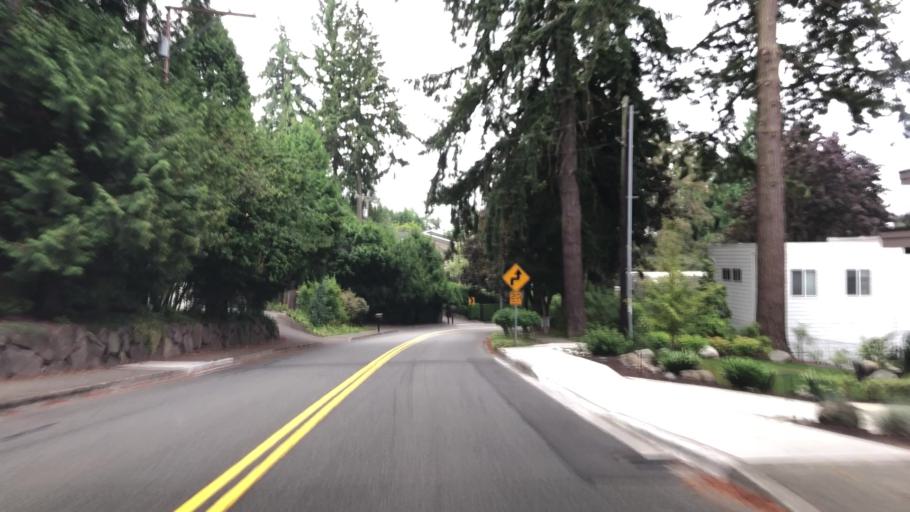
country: US
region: Washington
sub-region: King County
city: Kirkland
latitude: 47.6875
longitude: -122.1900
